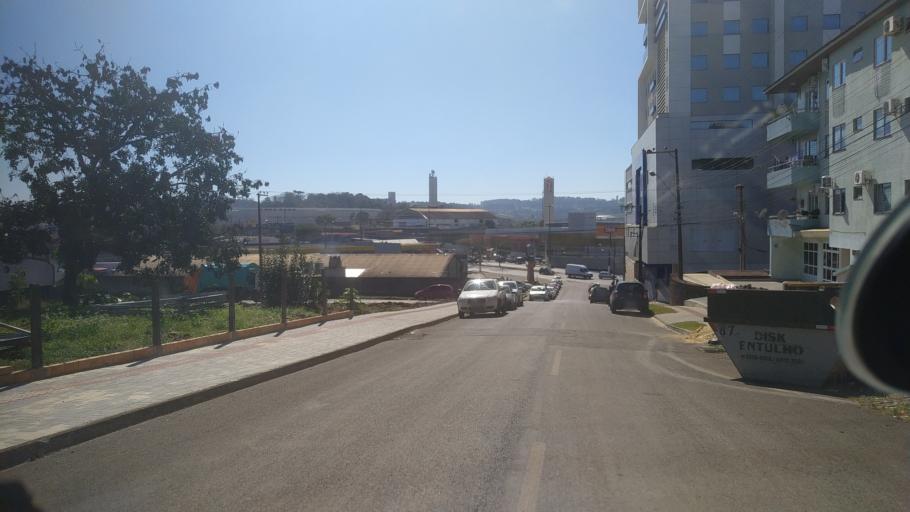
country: BR
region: Santa Catarina
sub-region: Chapeco
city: Chapeco
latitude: -27.0744
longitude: -52.6274
